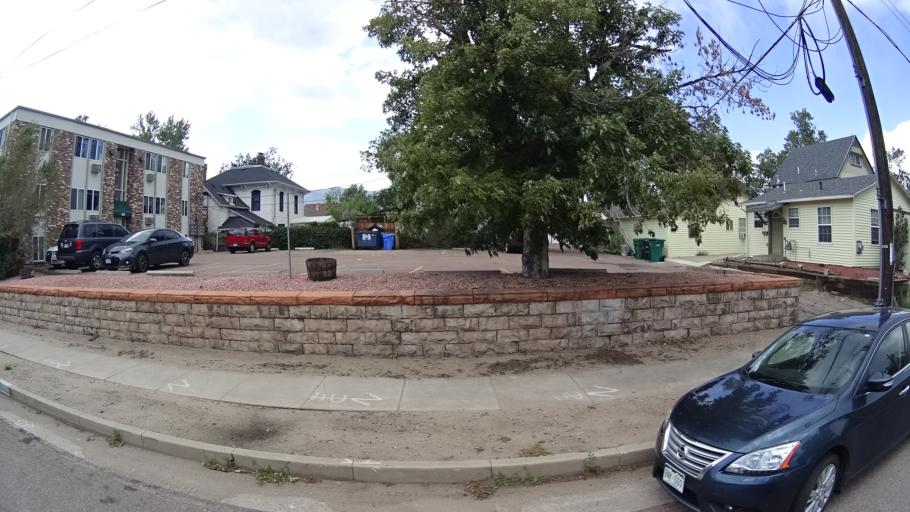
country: US
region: Colorado
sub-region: El Paso County
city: Colorado Springs
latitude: 38.8354
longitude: -104.8081
